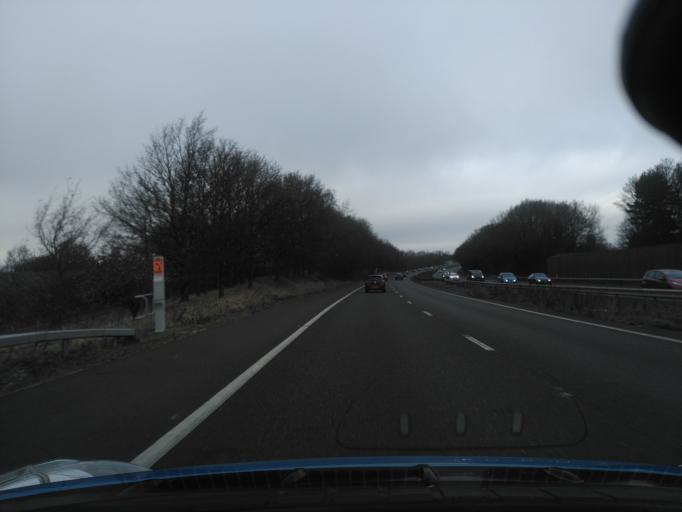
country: GB
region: England
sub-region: Hertfordshire
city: Stevenage
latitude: 51.9064
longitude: -0.2262
